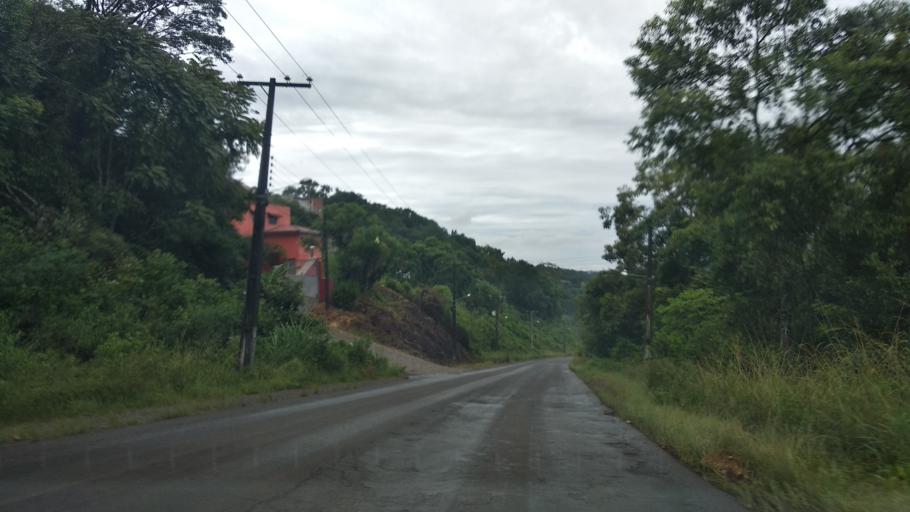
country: BR
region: Santa Catarina
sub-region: Videira
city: Videira
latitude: -26.9983
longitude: -51.1780
